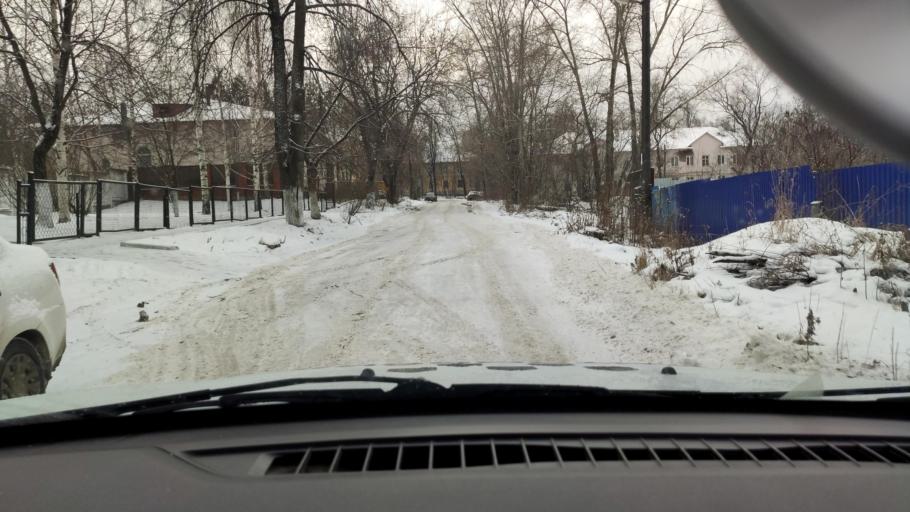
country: RU
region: Perm
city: Polazna
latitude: 58.1281
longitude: 56.3782
